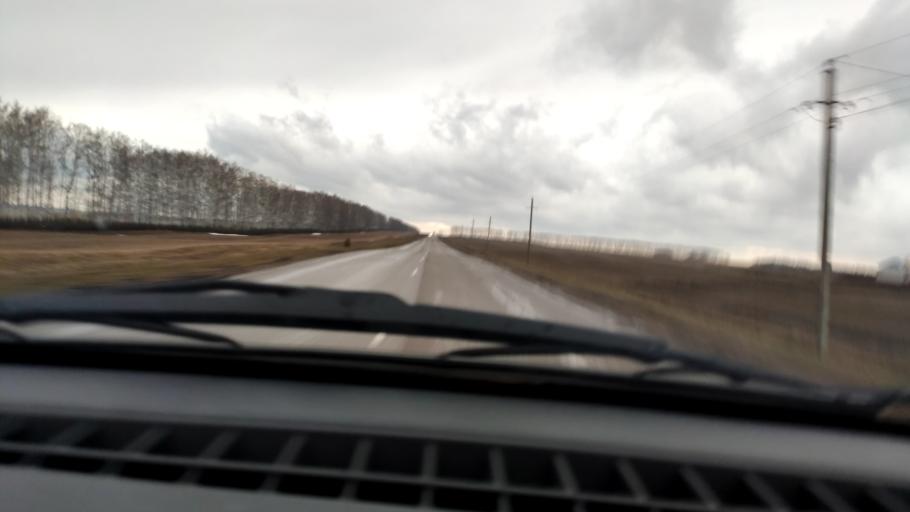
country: RU
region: Bashkortostan
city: Chekmagush
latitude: 55.1395
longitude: 54.6131
